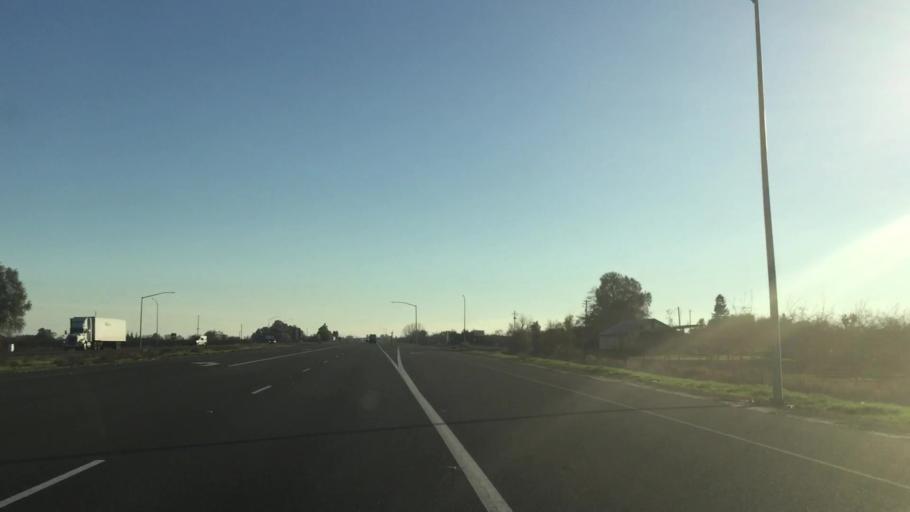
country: US
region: California
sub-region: Yuba County
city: Plumas Lake
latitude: 38.9556
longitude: -121.5439
